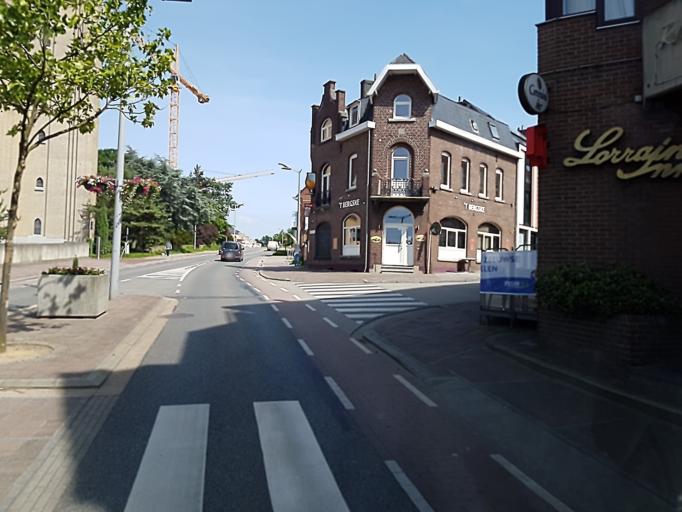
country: BE
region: Flanders
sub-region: Provincie Limburg
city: Genk
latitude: 50.9635
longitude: 5.4996
